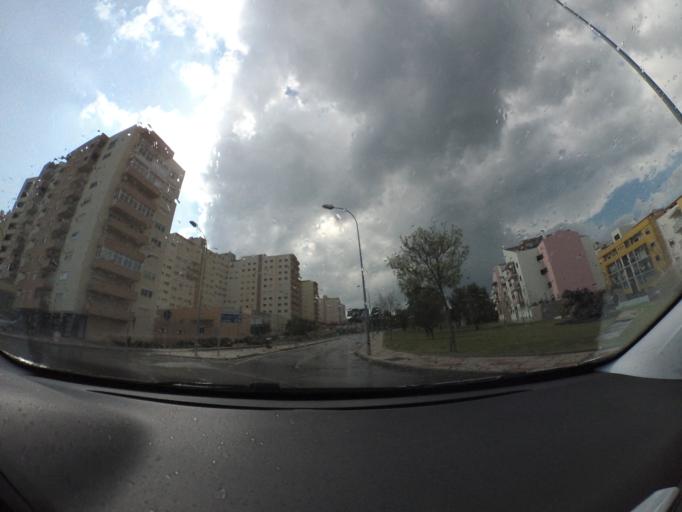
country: PT
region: Lisbon
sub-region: Oeiras
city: Linda-a-Velha
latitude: 38.7205
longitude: -9.2277
